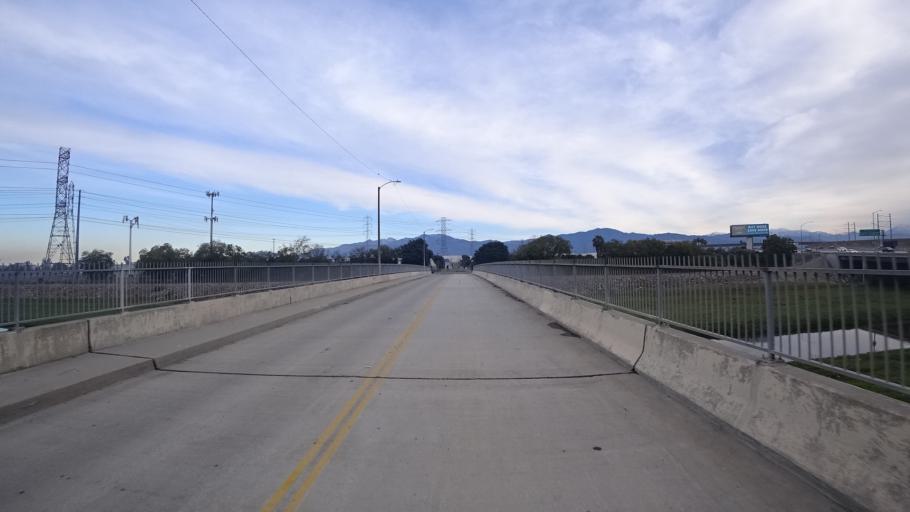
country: US
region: California
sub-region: Los Angeles County
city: Avocado Heights
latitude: 34.0605
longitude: -118.0021
